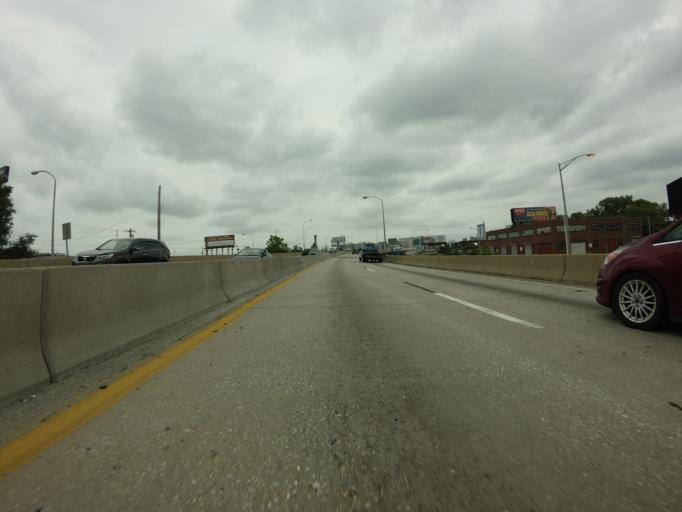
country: US
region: Pennsylvania
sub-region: Philadelphia County
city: Philadelphia
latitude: 39.9354
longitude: -75.1998
